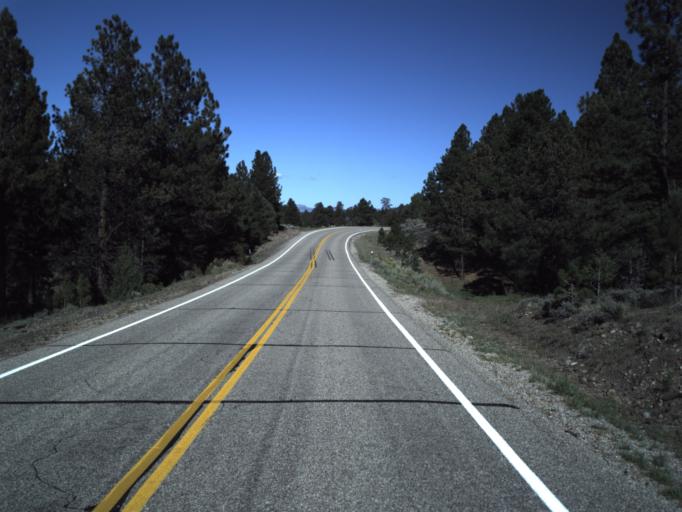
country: US
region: Utah
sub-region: Garfield County
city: Panguitch
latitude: 37.7472
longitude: -112.5785
